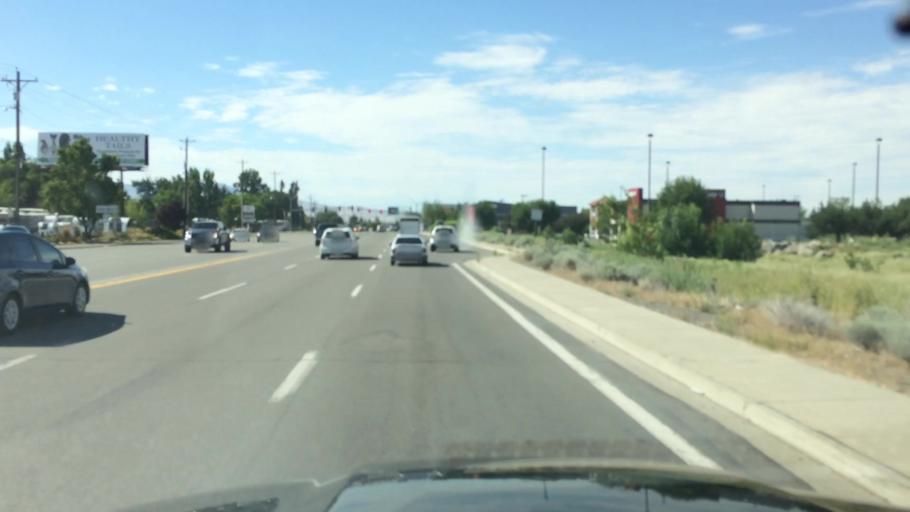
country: US
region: Nevada
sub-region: Washoe County
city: Sparks
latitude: 39.4399
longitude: -119.7700
